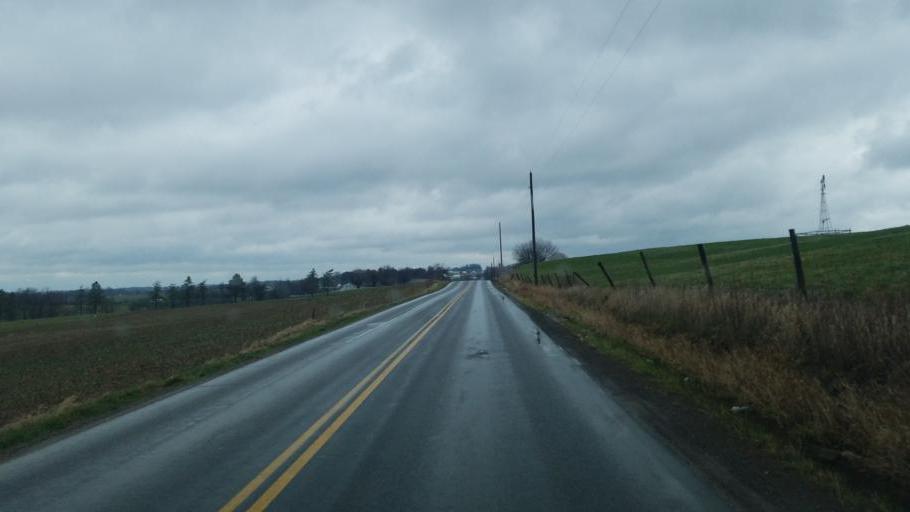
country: US
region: Ohio
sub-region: Holmes County
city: Millersburg
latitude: 40.5611
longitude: -81.7818
